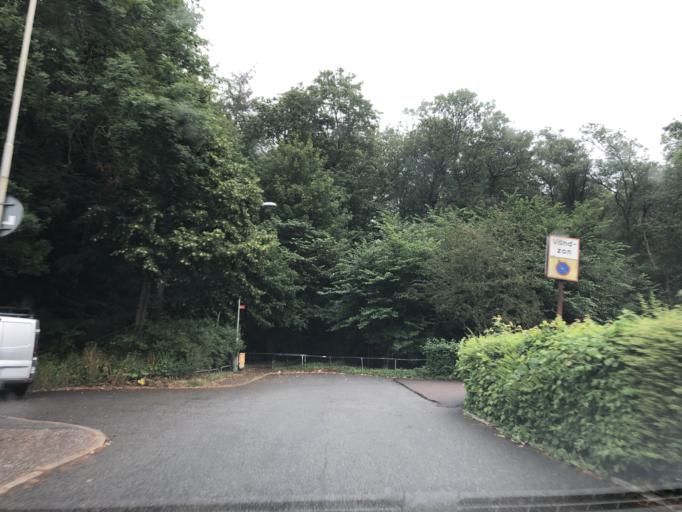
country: SE
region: Vaestra Goetaland
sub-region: Goteborg
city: Goeteborg
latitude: 57.7321
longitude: 11.9344
